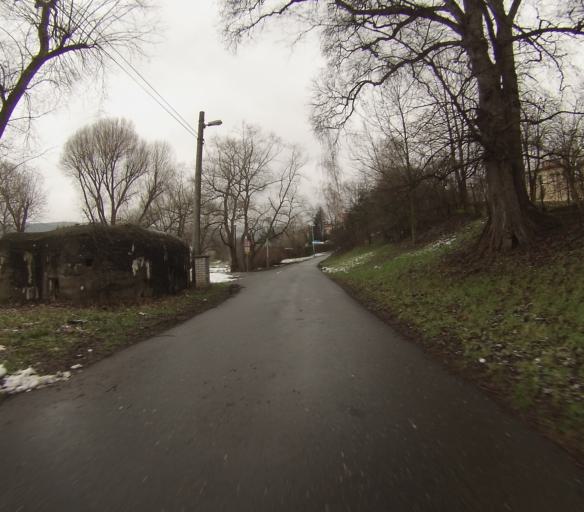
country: CZ
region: Ustecky
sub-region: Okres Decin
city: Decin
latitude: 50.7674
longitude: 14.2132
